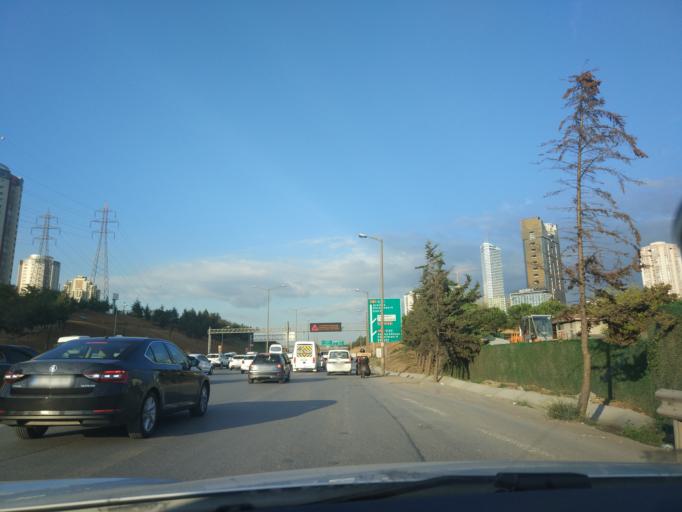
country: TR
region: Istanbul
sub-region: Atasehir
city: Atasehir
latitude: 40.9876
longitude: 29.1085
